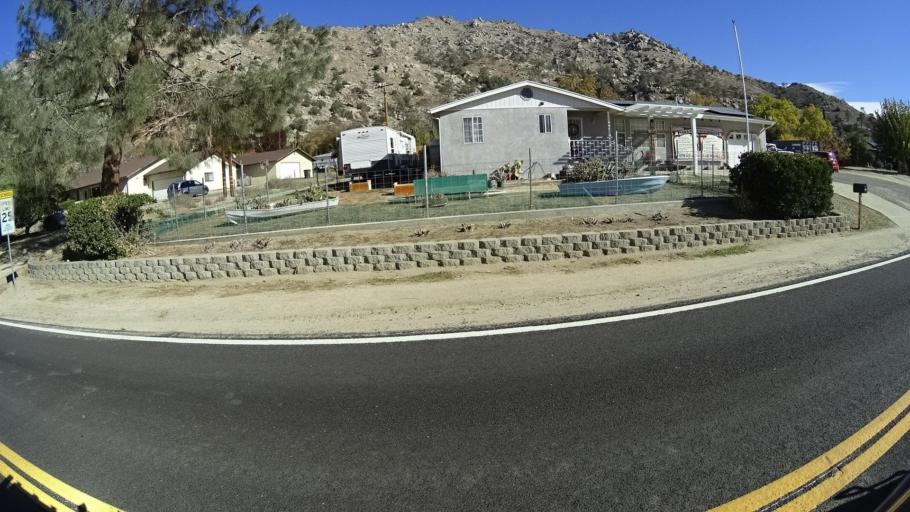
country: US
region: California
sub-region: Kern County
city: Lake Isabella
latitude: 35.6051
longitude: -118.4615
